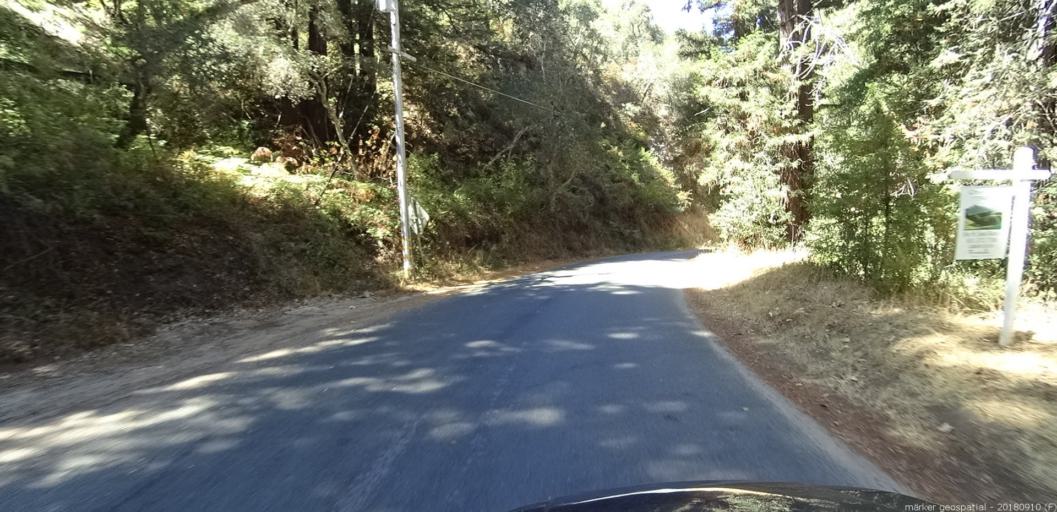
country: US
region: California
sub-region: Monterey County
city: Carmel Valley Village
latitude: 36.5130
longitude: -121.8119
